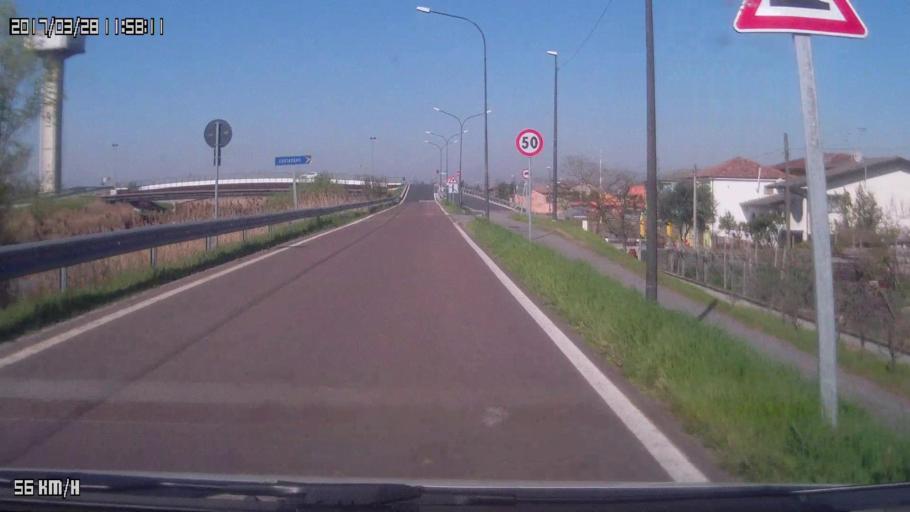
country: IT
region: Veneto
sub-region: Provincia di Venezia
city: Boscochiaro
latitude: 45.1390
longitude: 12.1183
